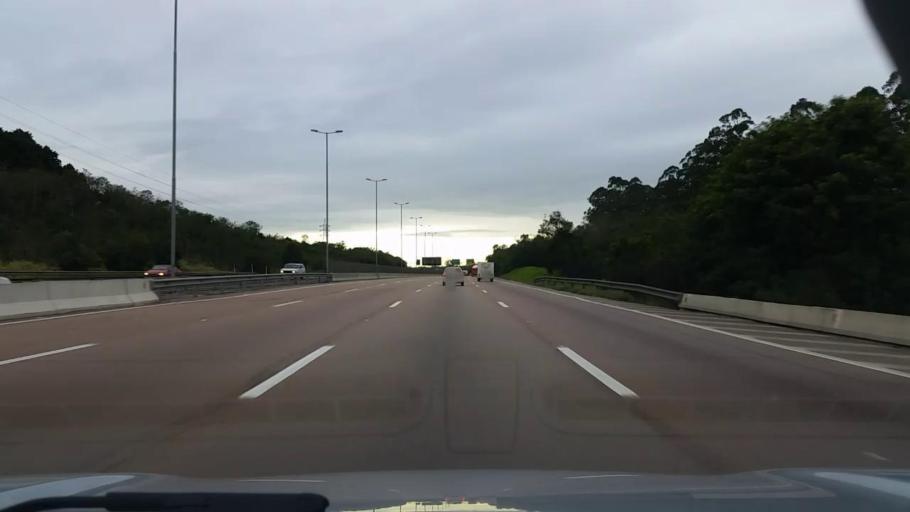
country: BR
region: Rio Grande do Sul
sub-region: Gravatai
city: Gravatai
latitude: -29.9555
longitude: -51.0256
